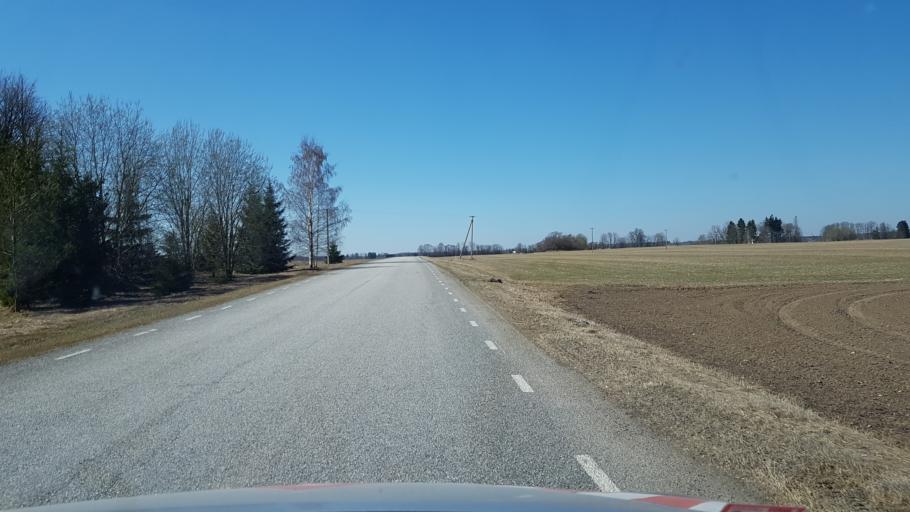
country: EE
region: Laeaene-Virumaa
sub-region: Rakke vald
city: Rakke
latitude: 59.0562
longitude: 26.4503
